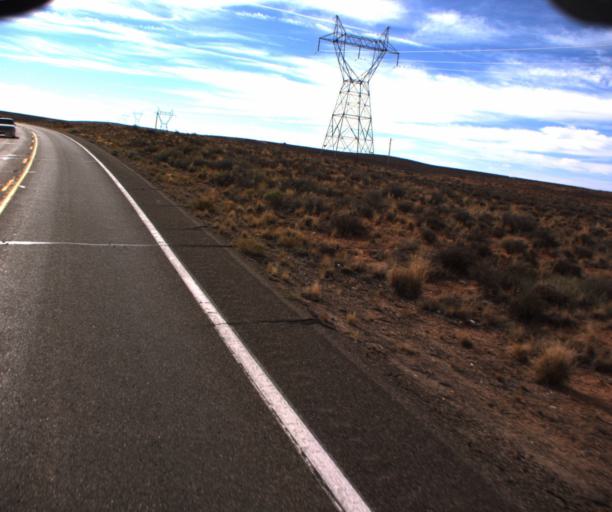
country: US
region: Arizona
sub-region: Coconino County
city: LeChee
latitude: 36.8442
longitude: -111.3291
